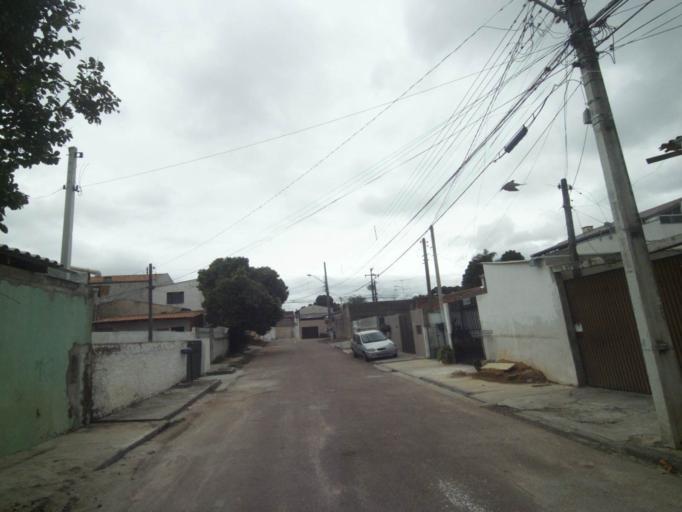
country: BR
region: Parana
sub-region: Curitiba
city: Curitiba
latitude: -25.4886
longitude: -49.3019
